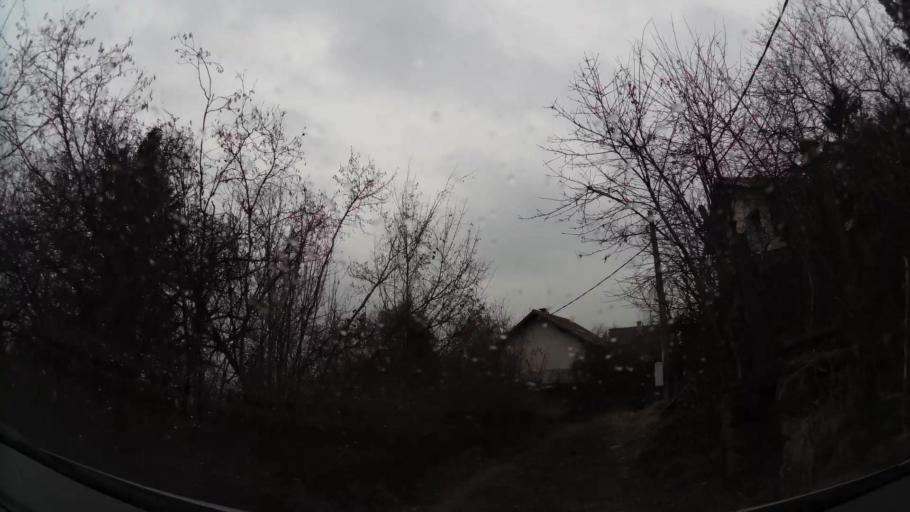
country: BG
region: Sofia-Capital
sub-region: Stolichna Obshtina
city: Sofia
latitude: 42.6002
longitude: 23.3885
